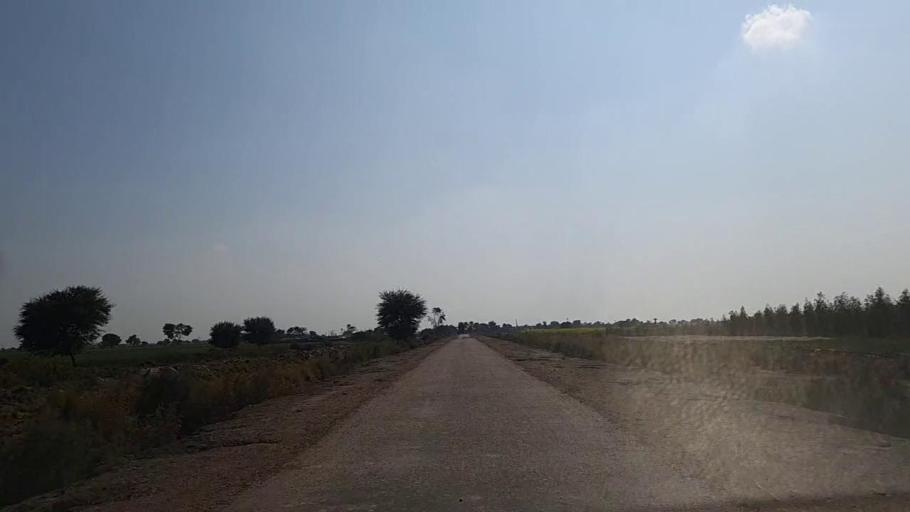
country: PK
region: Sindh
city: Jam Sahib
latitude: 26.2484
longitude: 68.5668
